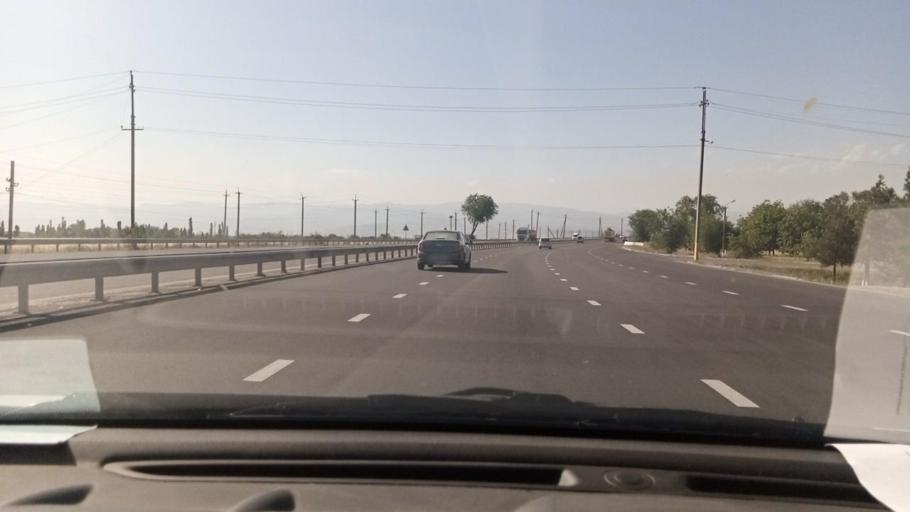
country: UZ
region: Toshkent
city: Ohangaron
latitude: 40.9298
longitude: 69.5953
